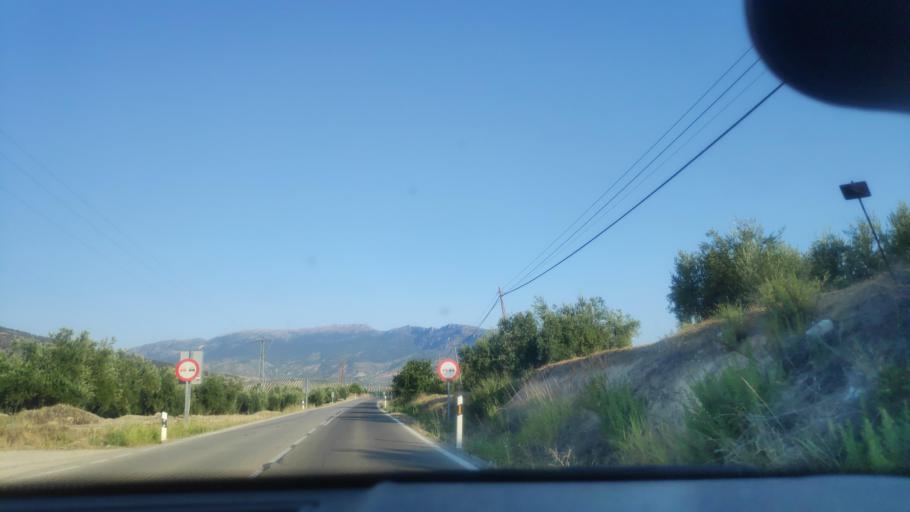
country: ES
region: Andalusia
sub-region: Provincia de Jaen
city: Jaen
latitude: 37.7368
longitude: -3.7716
